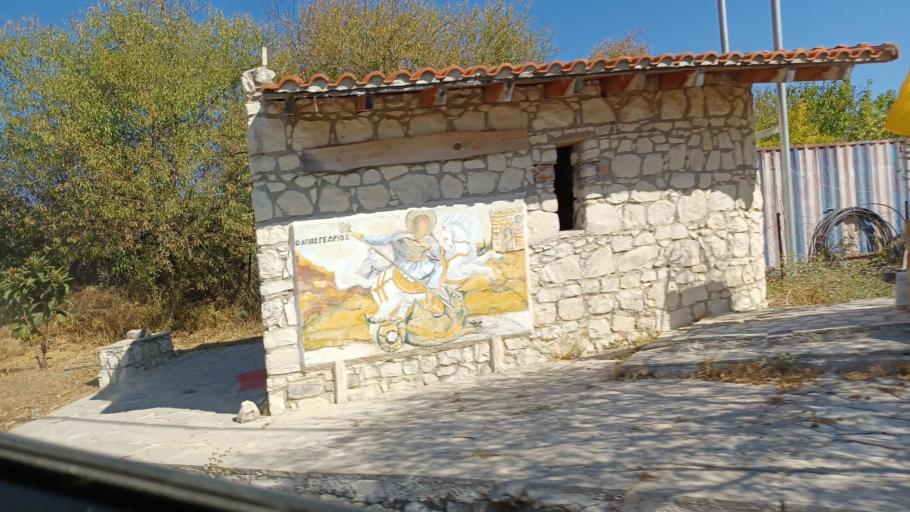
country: CY
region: Pafos
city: Mesogi
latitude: 34.9225
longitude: 32.5716
